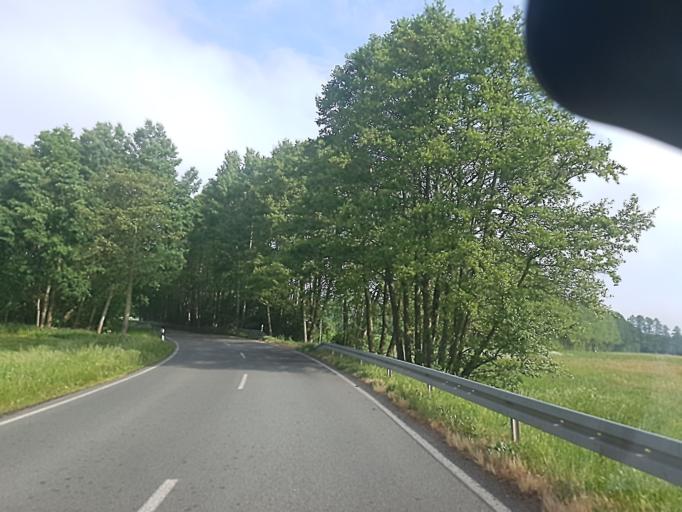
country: DE
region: Saxony-Anhalt
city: Rodleben
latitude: 52.0153
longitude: 12.2314
